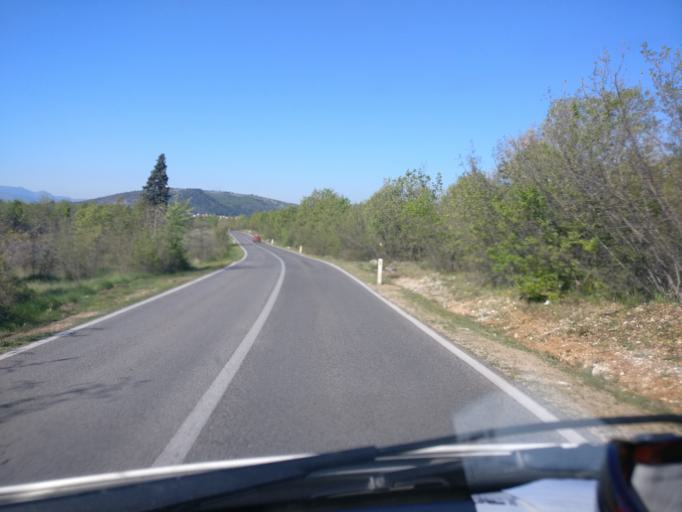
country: BA
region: Federation of Bosnia and Herzegovina
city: Tasovcici
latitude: 43.1307
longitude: 17.7675
